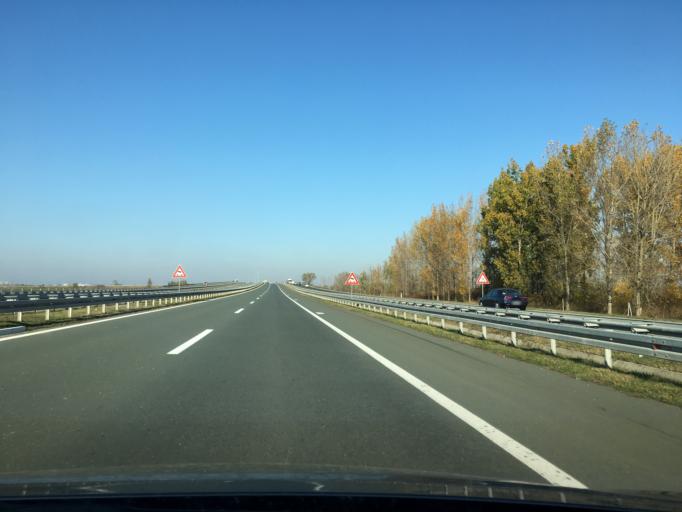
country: RS
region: Autonomna Pokrajina Vojvodina
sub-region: Juznobacki Okrug
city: Petrovaradin
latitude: 45.2972
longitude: 19.8748
